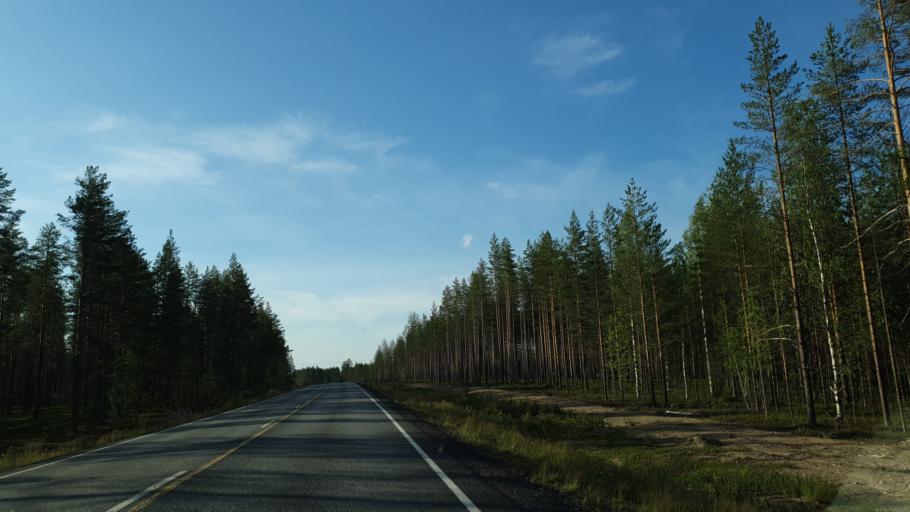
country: FI
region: Kainuu
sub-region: Kehys-Kainuu
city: Kuhmo
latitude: 64.0894
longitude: 29.4816
